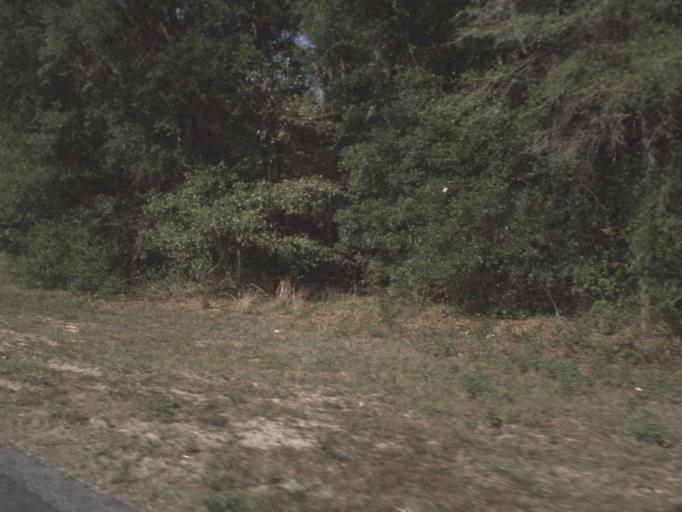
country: US
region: Florida
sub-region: Marion County
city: Dunnellon
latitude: 29.1197
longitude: -82.4469
